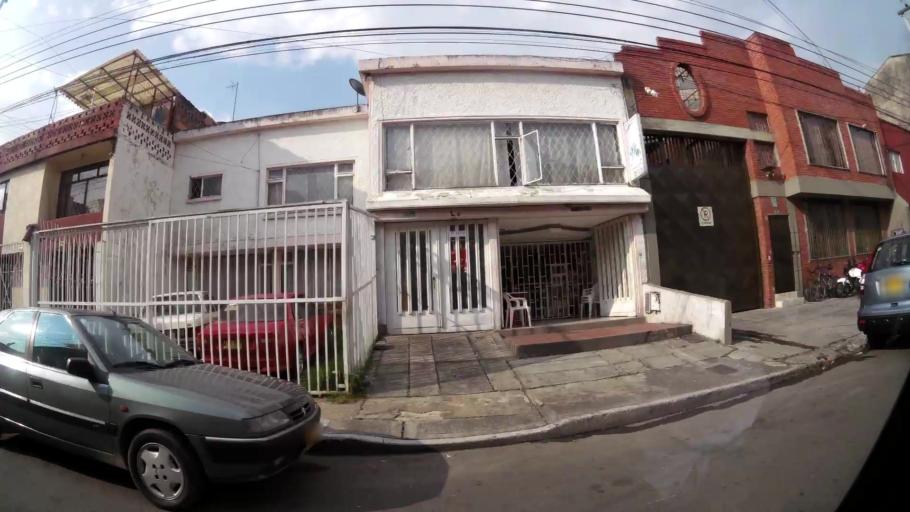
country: CO
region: Bogota D.C.
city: Barrio San Luis
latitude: 4.7226
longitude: -74.0583
